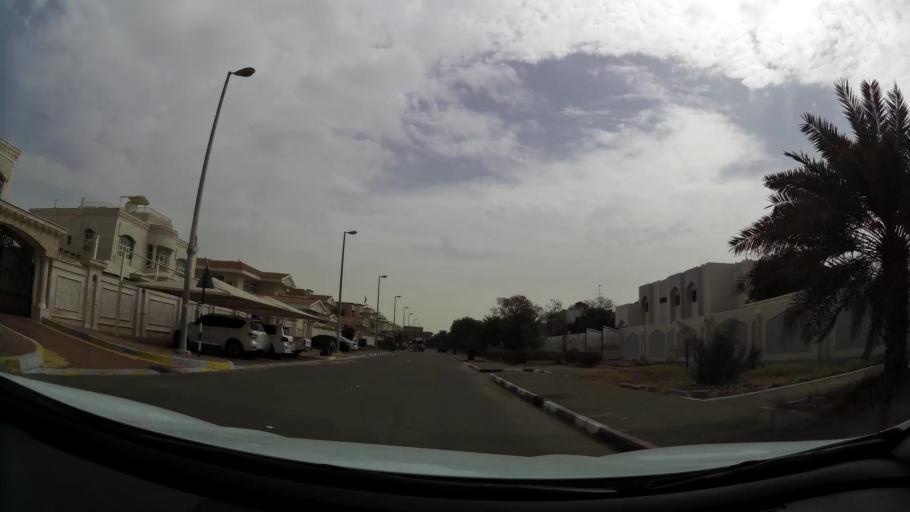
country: AE
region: Abu Dhabi
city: Abu Dhabi
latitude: 24.3938
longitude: 54.5027
